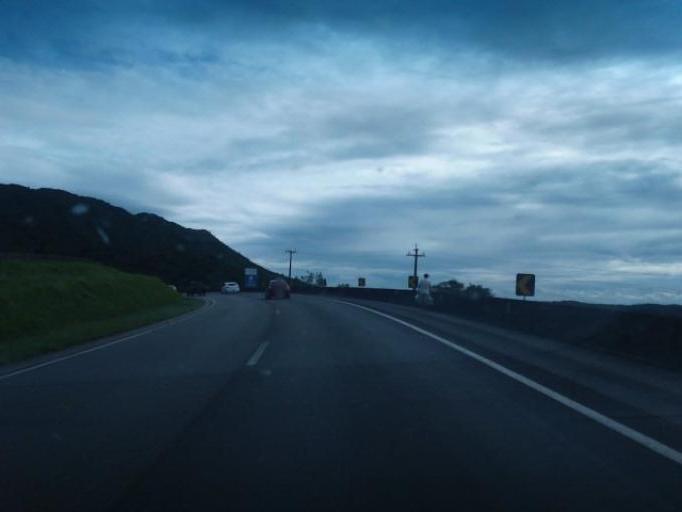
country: BR
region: Parana
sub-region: Campina Grande Do Sul
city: Campina Grande do Sul
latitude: -25.1595
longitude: -48.8622
